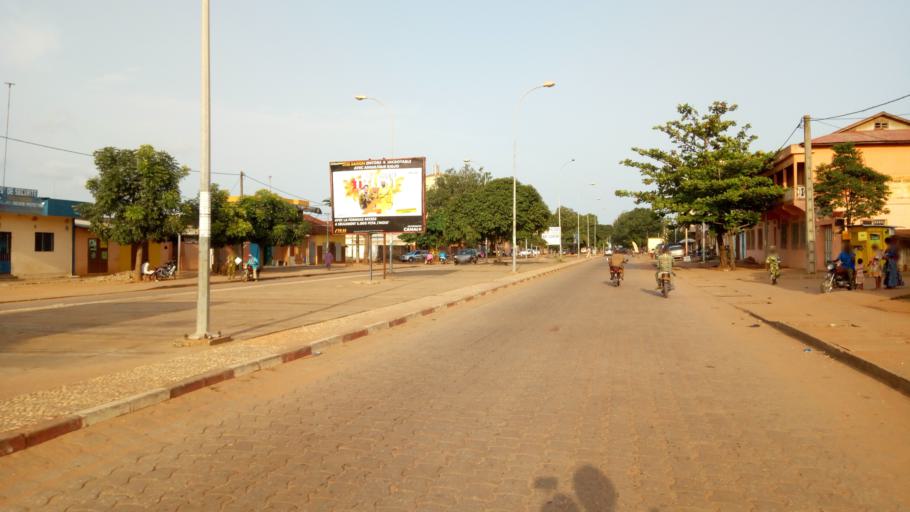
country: BJ
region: Queme
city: Porto-Novo
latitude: 6.4847
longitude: 2.6220
